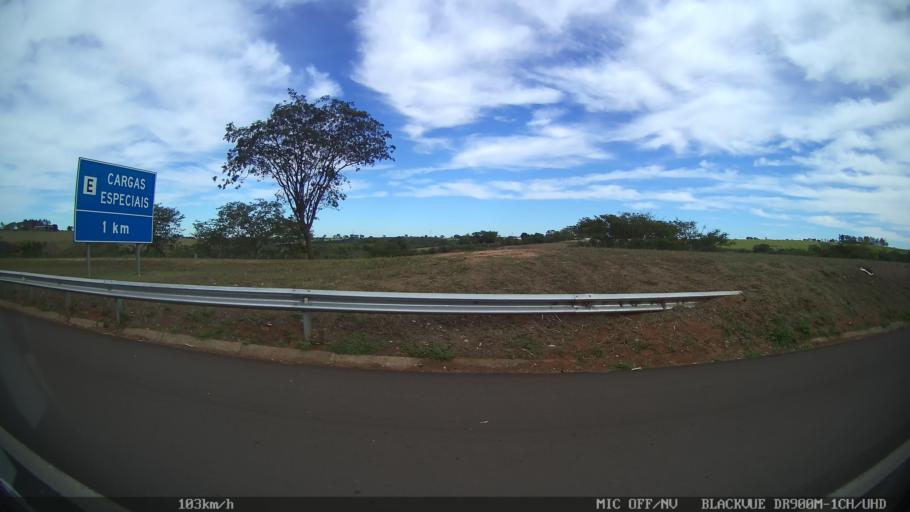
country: BR
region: Sao Paulo
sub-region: Santa Adelia
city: Santa Adelia
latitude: -21.2956
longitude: -48.8394
